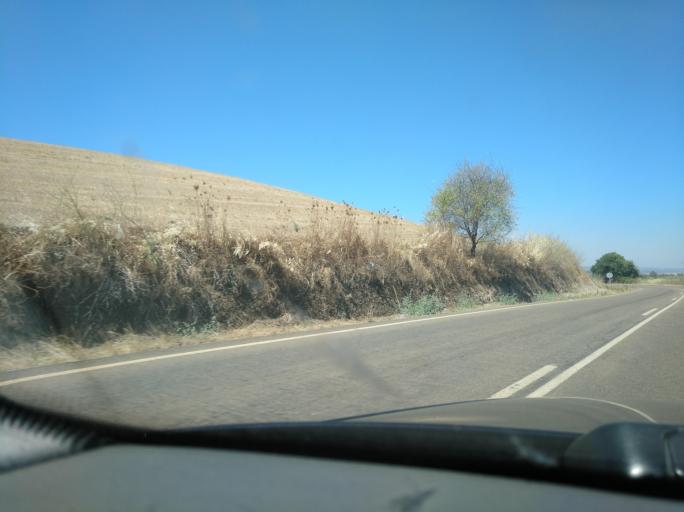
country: ES
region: Extremadura
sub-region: Provincia de Badajoz
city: Olivenza
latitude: 38.6969
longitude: -7.1334
